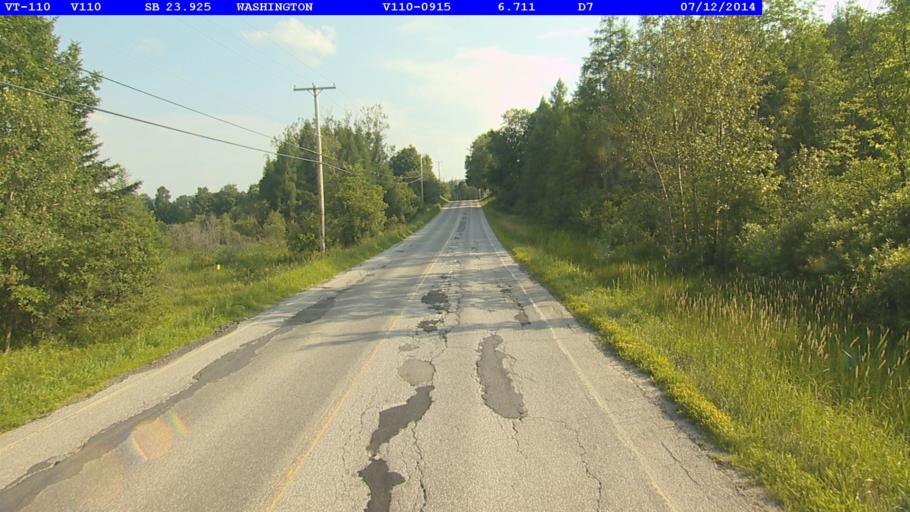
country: US
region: Vermont
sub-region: Washington County
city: South Barre
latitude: 44.1199
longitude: -72.4323
